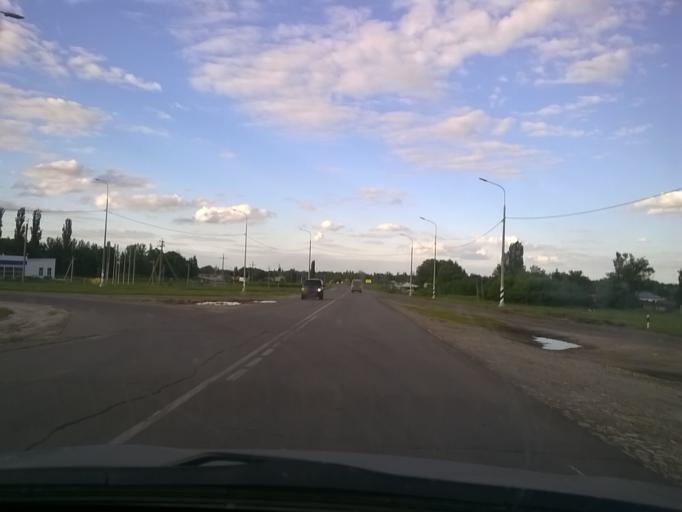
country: RU
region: Volgograd
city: Novonikolayevskiy
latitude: 50.9485
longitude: 42.3301
